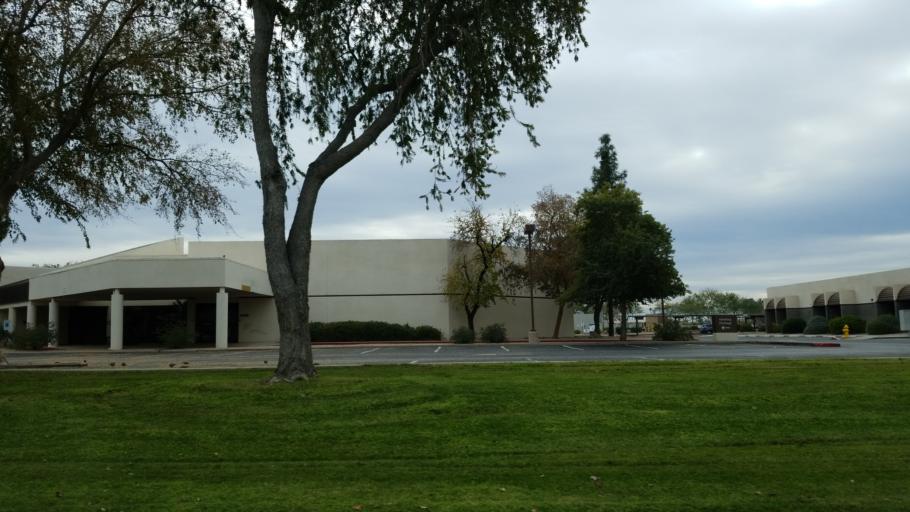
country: US
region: Arizona
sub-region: Maricopa County
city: Sun City
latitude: 33.6050
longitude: -112.2872
